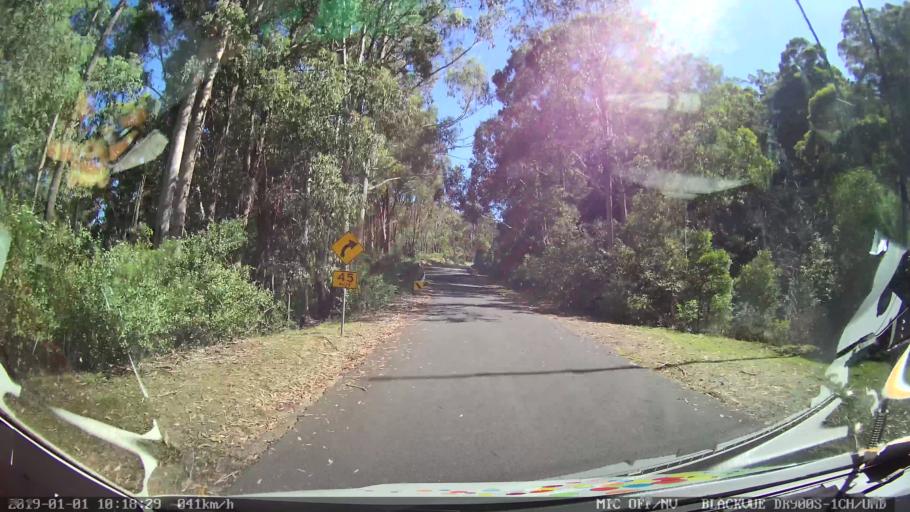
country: AU
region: New South Wales
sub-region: Snowy River
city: Jindabyne
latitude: -36.0883
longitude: 148.1821
